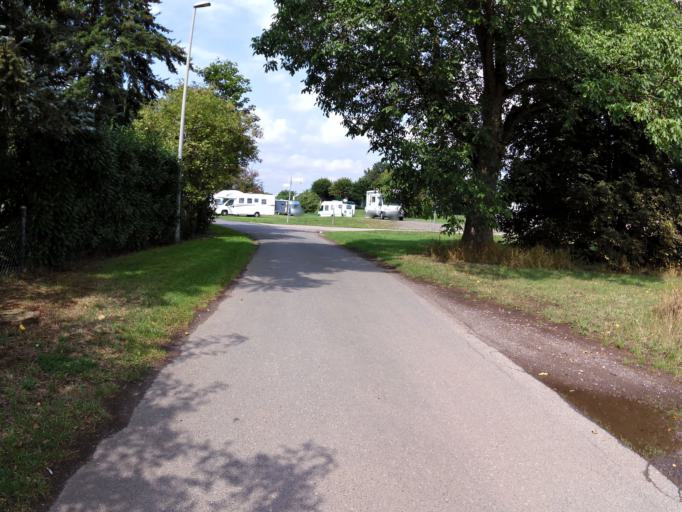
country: DE
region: Lower Saxony
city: Hoya
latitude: 52.7995
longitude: 9.1460
